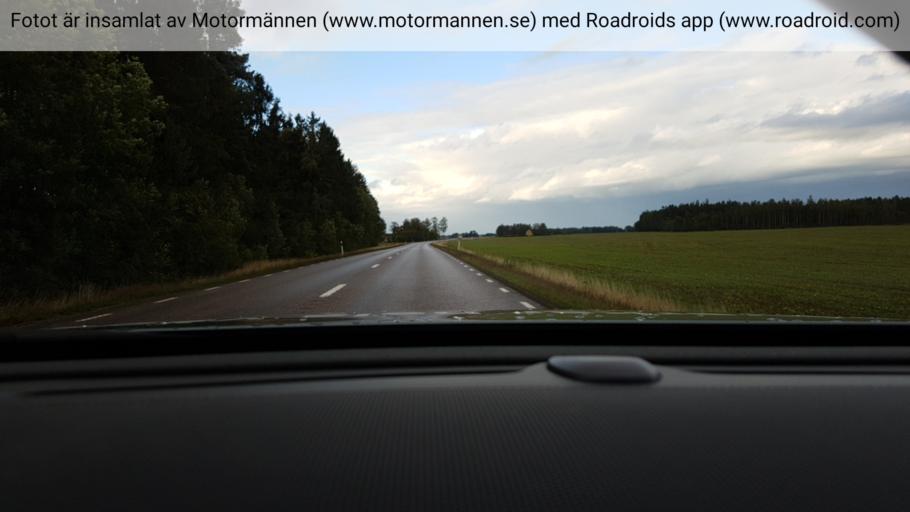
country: SE
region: Vaestra Goetaland
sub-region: Vanersborgs Kommun
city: Bralanda
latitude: 58.6107
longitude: 12.4152
